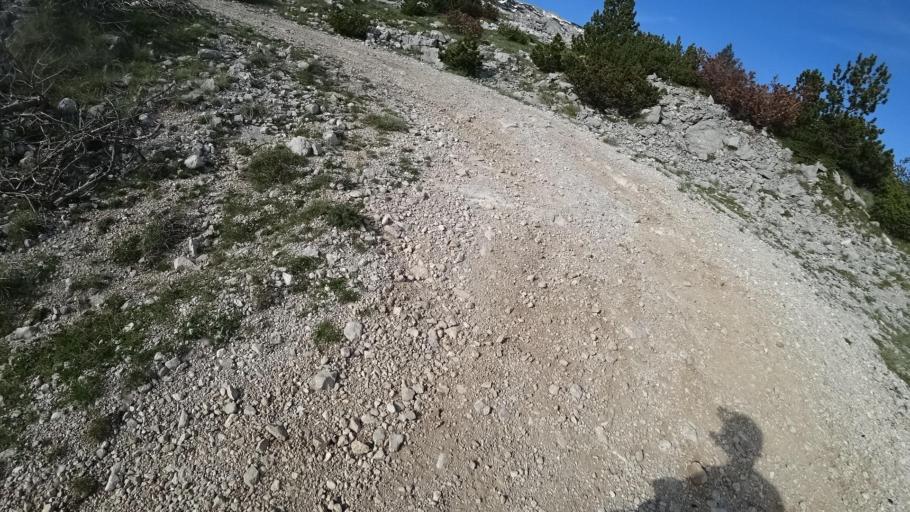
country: BA
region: Federation of Bosnia and Herzegovina
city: Kocerin
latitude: 43.5752
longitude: 17.5399
